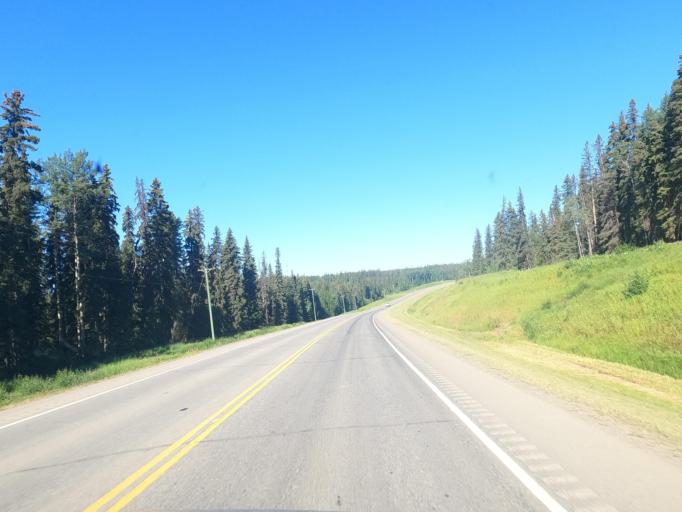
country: CA
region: British Columbia
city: Fort St. John
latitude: 56.6369
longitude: -121.6377
